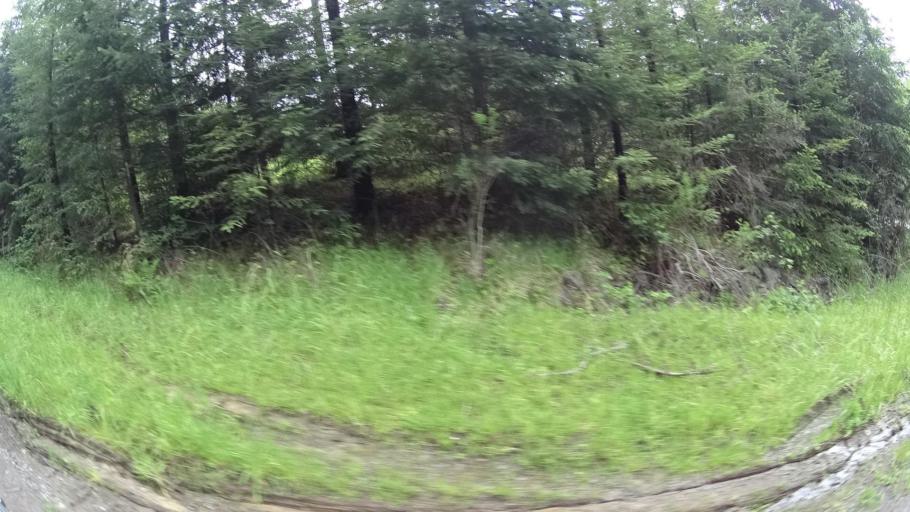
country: US
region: California
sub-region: Humboldt County
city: Blue Lake
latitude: 40.9042
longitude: -123.9865
